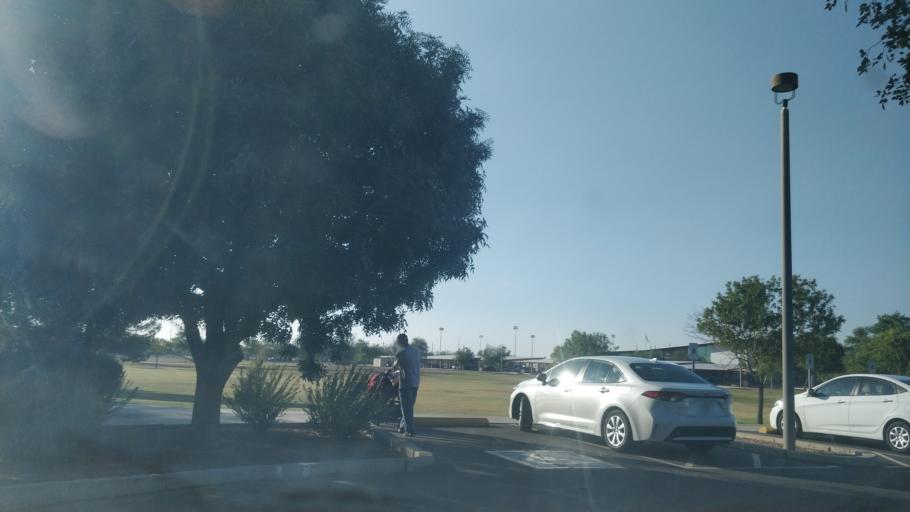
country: US
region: Arizona
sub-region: Maricopa County
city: Chandler
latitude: 33.2742
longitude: -111.8270
